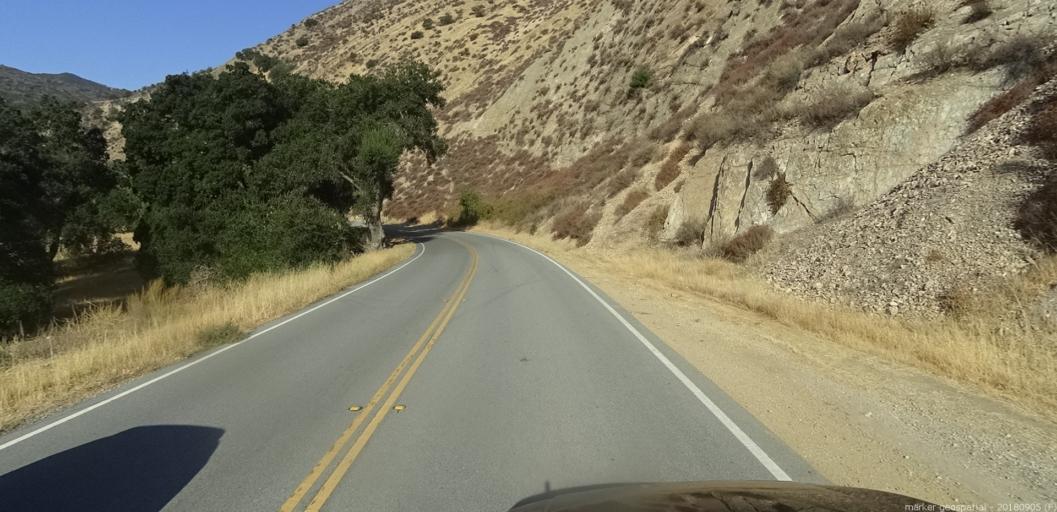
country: US
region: California
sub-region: Monterey County
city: Greenfield
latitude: 36.2576
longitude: -121.4280
